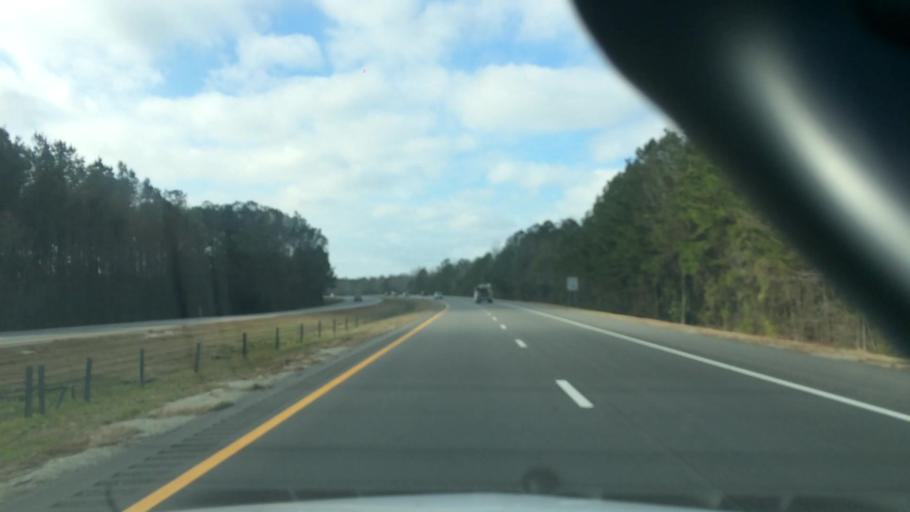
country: US
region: North Carolina
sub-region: New Hanover County
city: Wrightsboro
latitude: 34.3188
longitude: -77.9296
